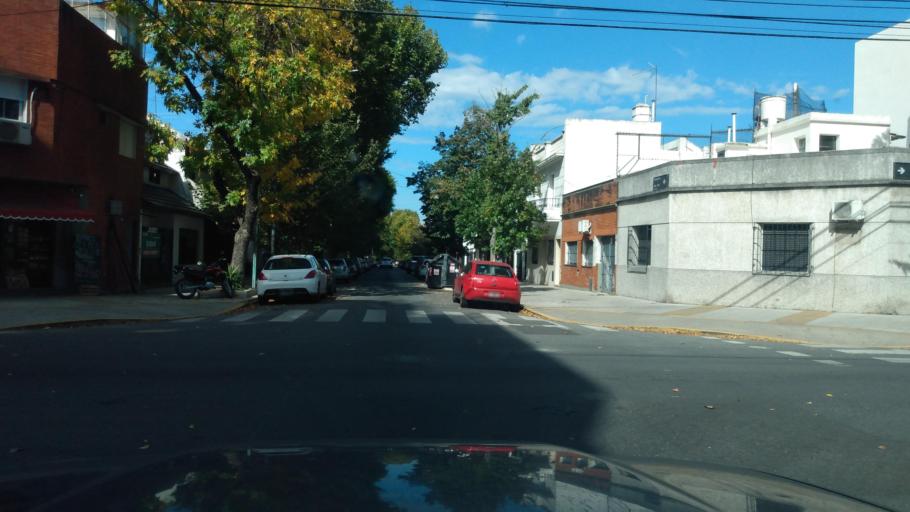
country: AR
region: Buenos Aires F.D.
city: Villa Santa Rita
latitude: -34.5810
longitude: -58.4877
